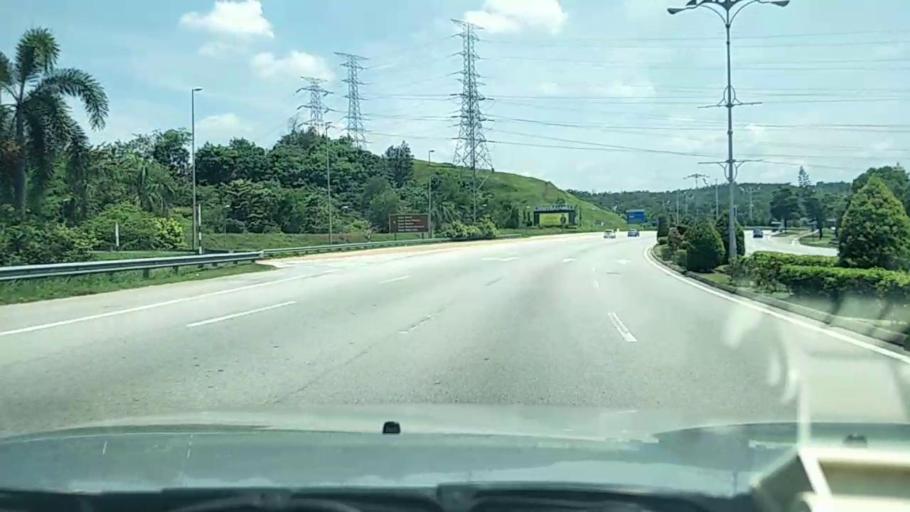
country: MY
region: Putrajaya
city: Putrajaya
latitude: 2.9591
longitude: 101.7168
